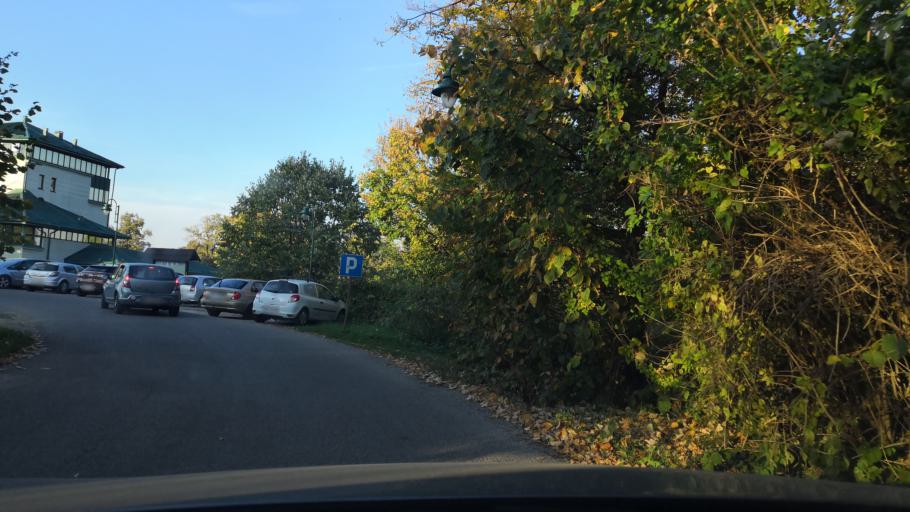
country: RS
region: Autonomna Pokrajina Vojvodina
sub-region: Sremski Okrug
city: Irig
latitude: 45.1584
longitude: 19.8631
